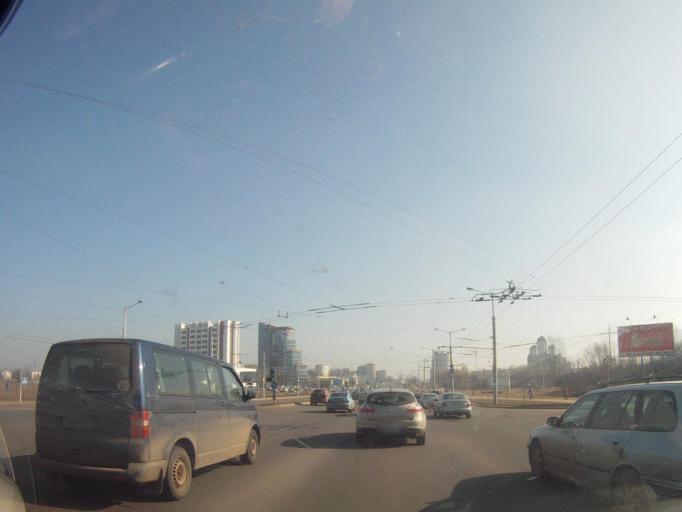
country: BY
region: Minsk
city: Novoye Medvezhino
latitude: 53.9069
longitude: 27.4620
